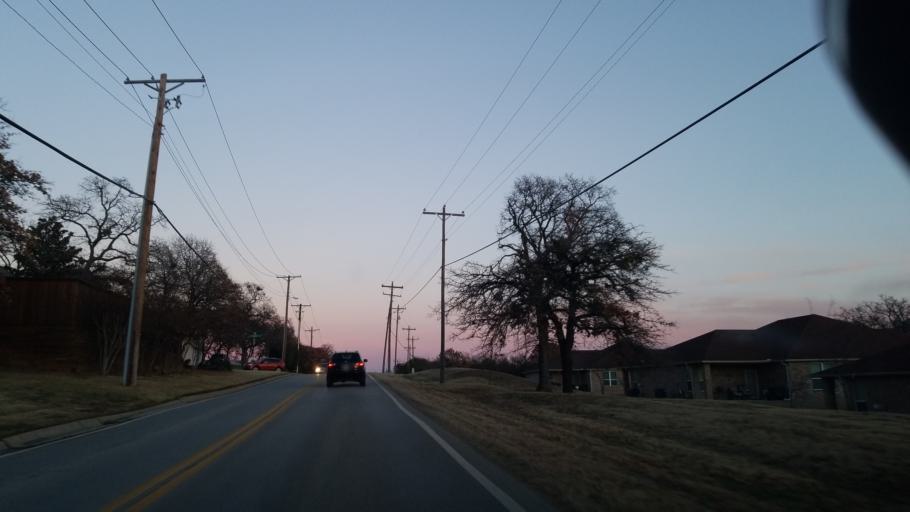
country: US
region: Texas
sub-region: Denton County
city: Denton
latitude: 33.1616
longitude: -97.1193
